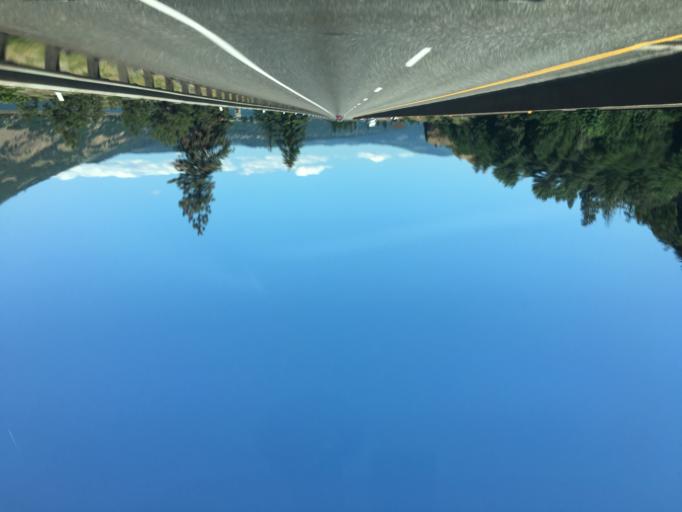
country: US
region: Washington
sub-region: Klickitat County
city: White Salmon
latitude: 45.6928
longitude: -121.4423
